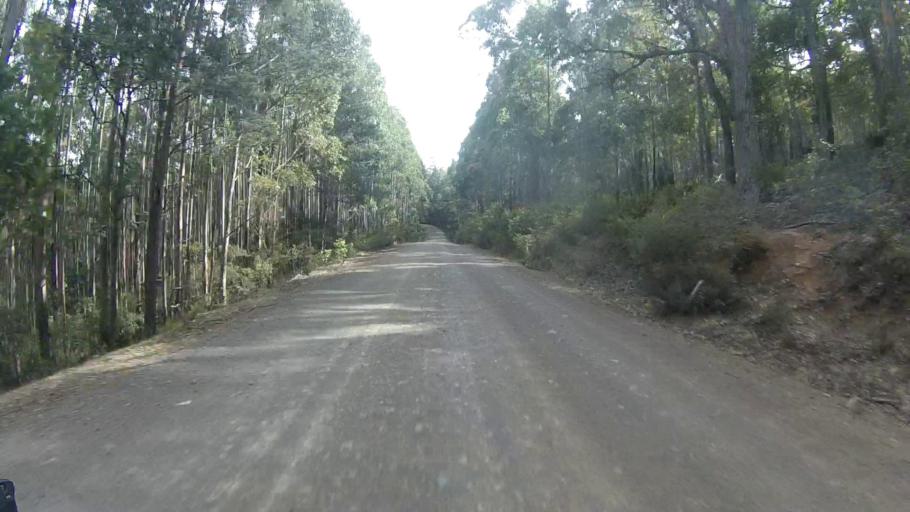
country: AU
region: Tasmania
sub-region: Sorell
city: Sorell
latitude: -42.7494
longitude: 147.8286
